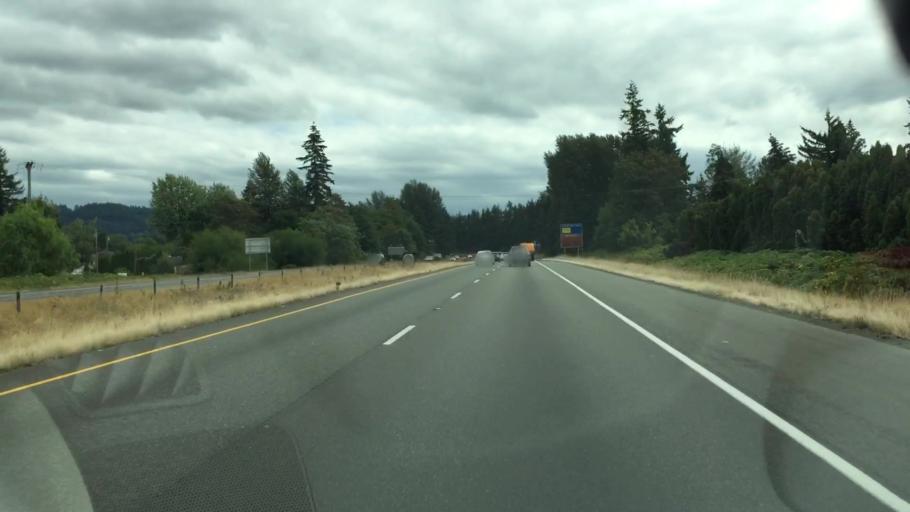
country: US
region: Washington
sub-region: Pierce County
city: Sumner
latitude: 47.1940
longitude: -122.2413
